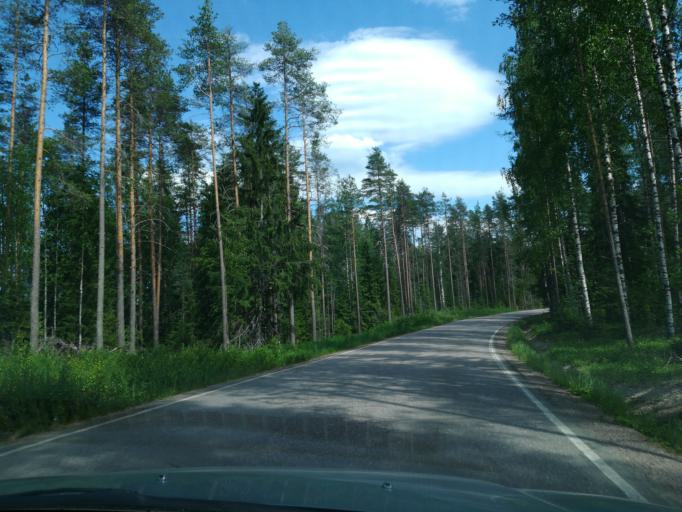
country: FI
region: South Karelia
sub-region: Imatra
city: Ruokolahti
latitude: 61.4755
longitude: 28.8021
